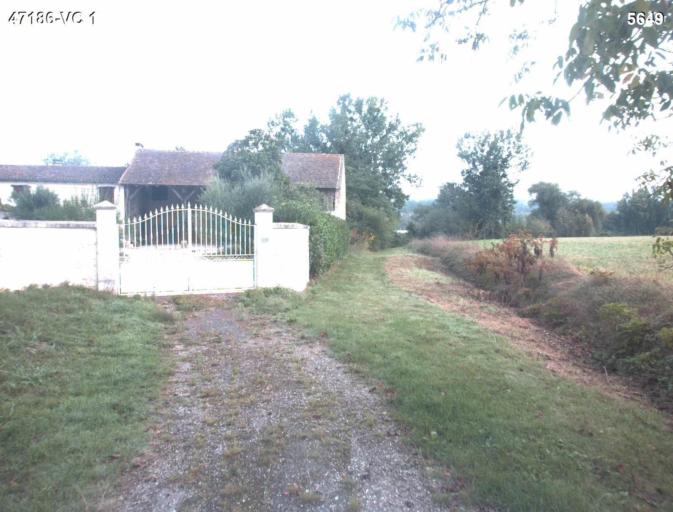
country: FR
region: Aquitaine
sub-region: Departement du Lot-et-Garonne
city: Port-Sainte-Marie
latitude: 44.2324
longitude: 0.4316
